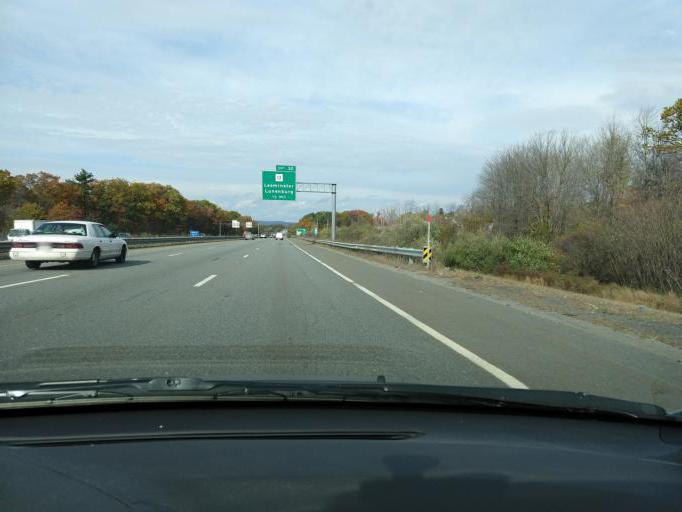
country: US
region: Massachusetts
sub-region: Worcester County
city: Leominster
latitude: 42.5301
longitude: -71.7348
